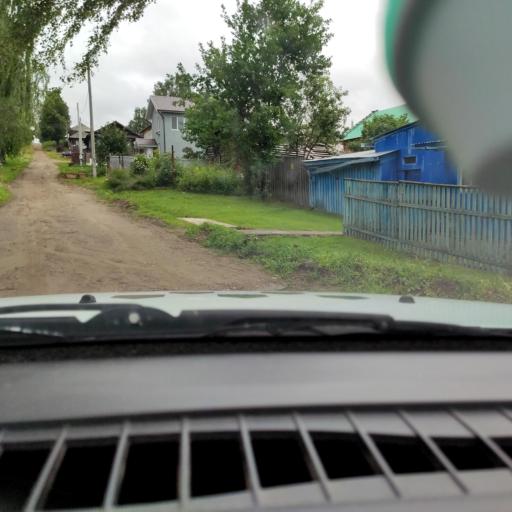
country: RU
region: Perm
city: Dobryanka
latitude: 58.4635
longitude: 56.4219
